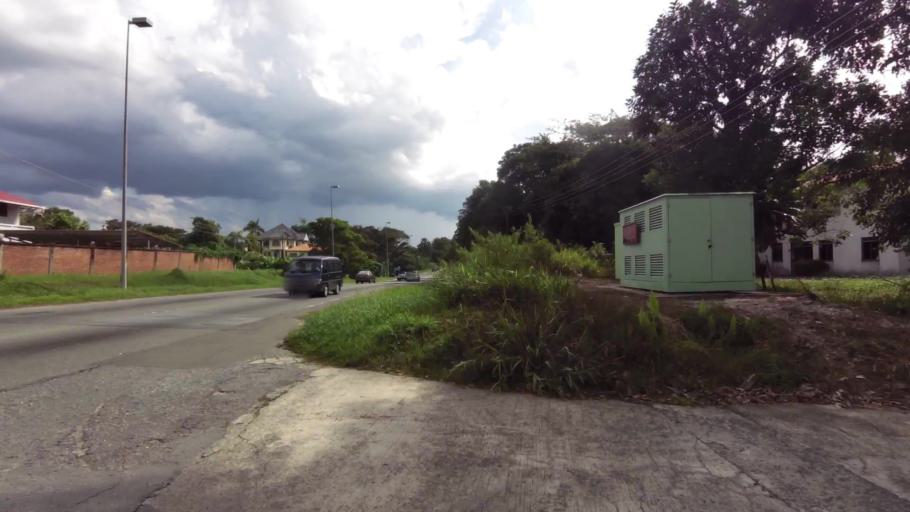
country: BN
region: Brunei and Muara
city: Bandar Seri Begawan
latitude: 4.9531
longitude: 114.9702
